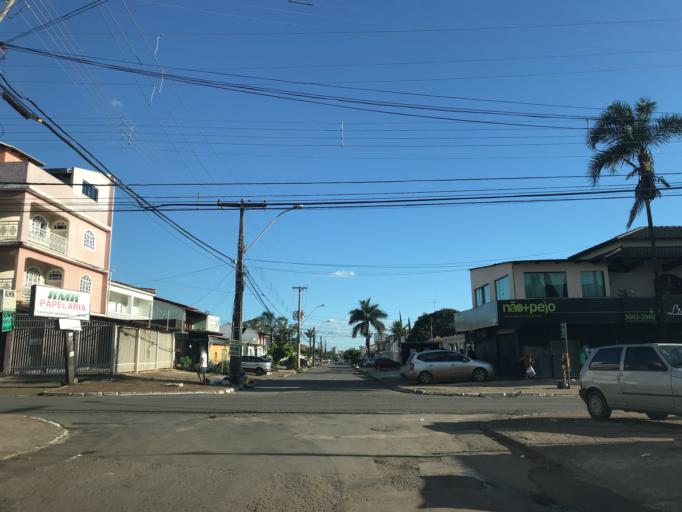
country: BR
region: Federal District
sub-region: Brasilia
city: Brasilia
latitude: -15.8112
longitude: -48.0639
